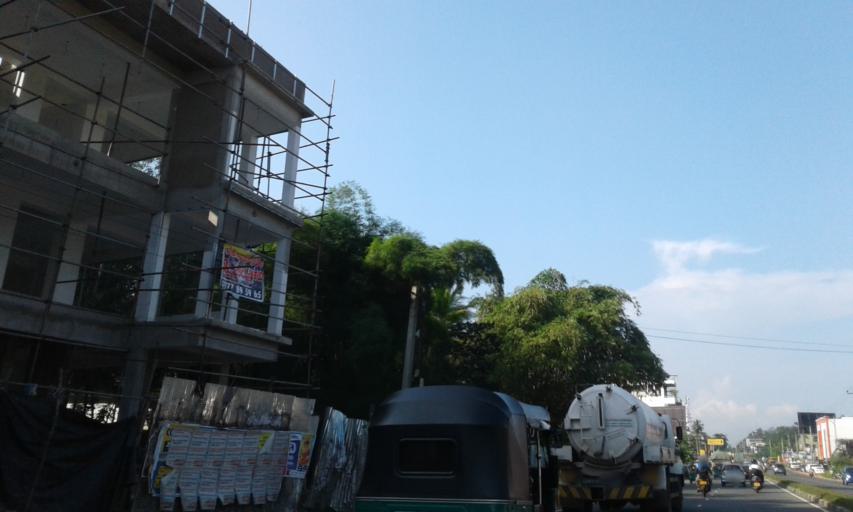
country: LK
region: Western
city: Gampaha
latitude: 7.0265
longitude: 79.9800
